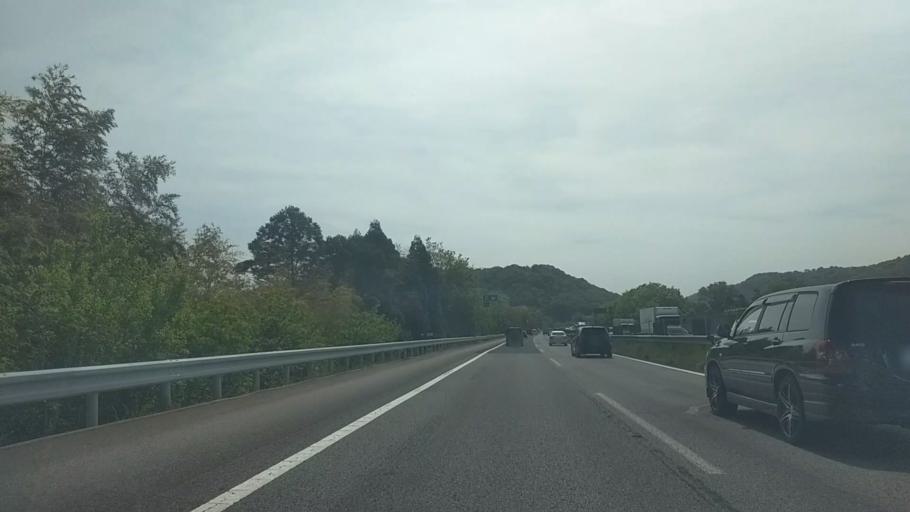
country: JP
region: Aichi
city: Okazaki
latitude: 34.9345
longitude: 137.2152
